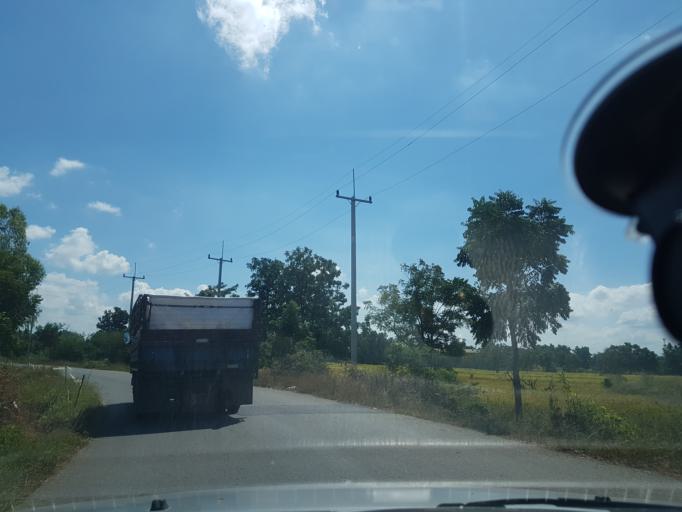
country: TH
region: Lop Buri
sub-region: Amphoe Tha Luang
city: Tha Luang
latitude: 14.9890
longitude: 101.0103
